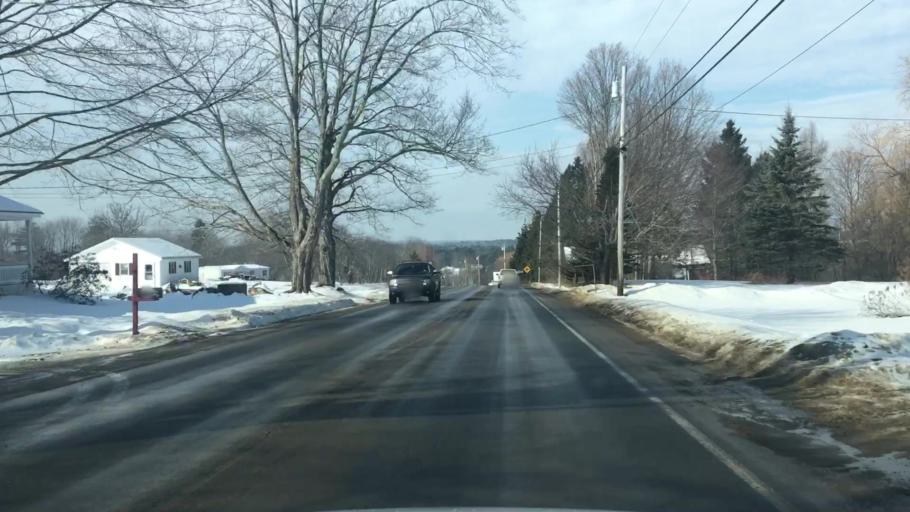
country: US
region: Maine
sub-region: Penobscot County
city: Hermon
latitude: 44.8475
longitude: -68.8724
